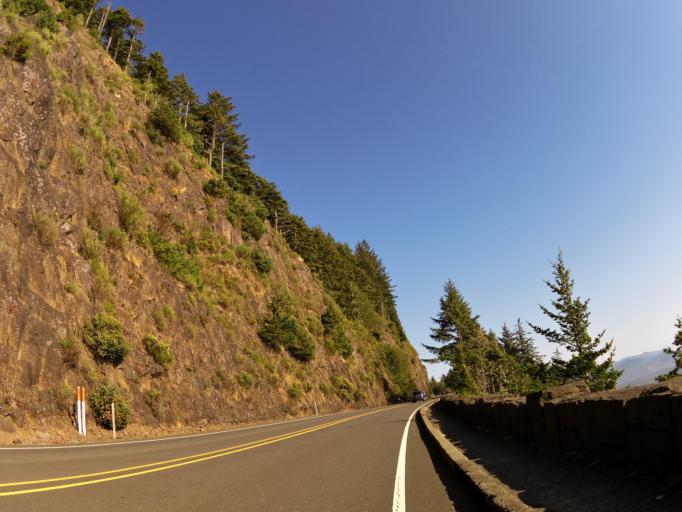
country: US
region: Oregon
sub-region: Tillamook County
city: Rockaway Beach
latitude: 45.7433
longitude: -123.9575
